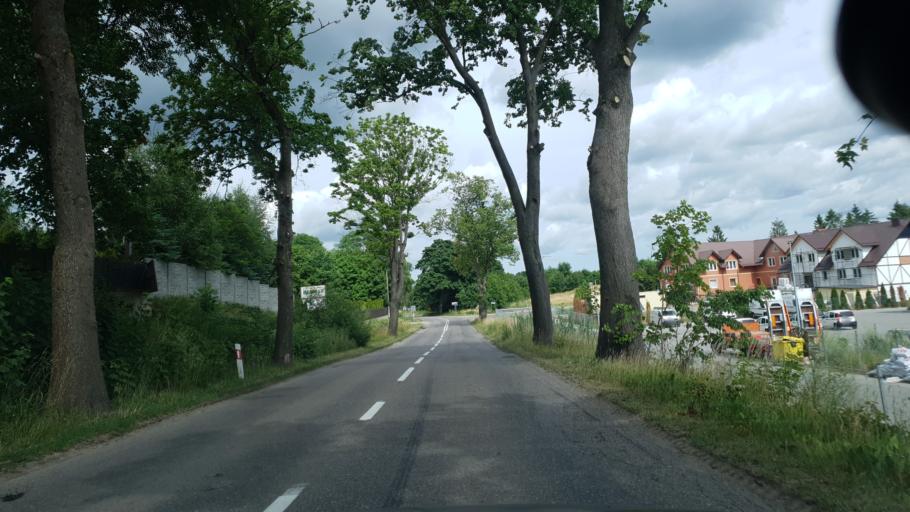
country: PL
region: Pomeranian Voivodeship
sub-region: Powiat kartuski
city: Kartuzy
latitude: 54.3536
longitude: 18.2251
